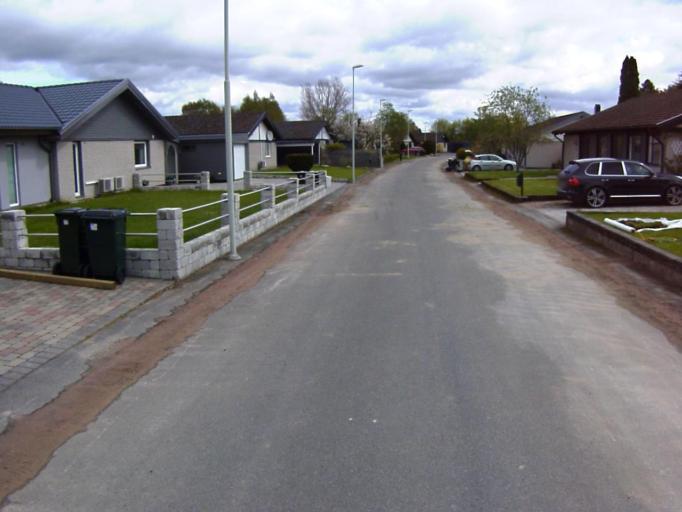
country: SE
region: Skane
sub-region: Kristianstads Kommun
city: Kristianstad
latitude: 56.0477
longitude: 14.1820
